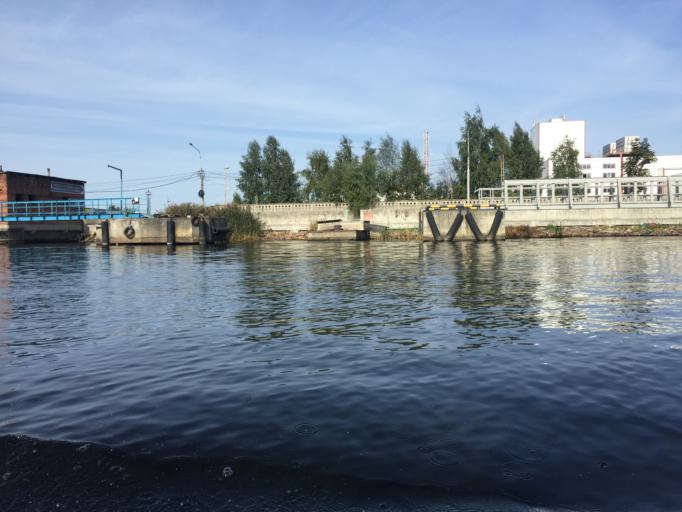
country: RU
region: Kaliningrad
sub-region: Gorod Kaliningrad
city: Kaliningrad
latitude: 54.7045
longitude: 20.4812
